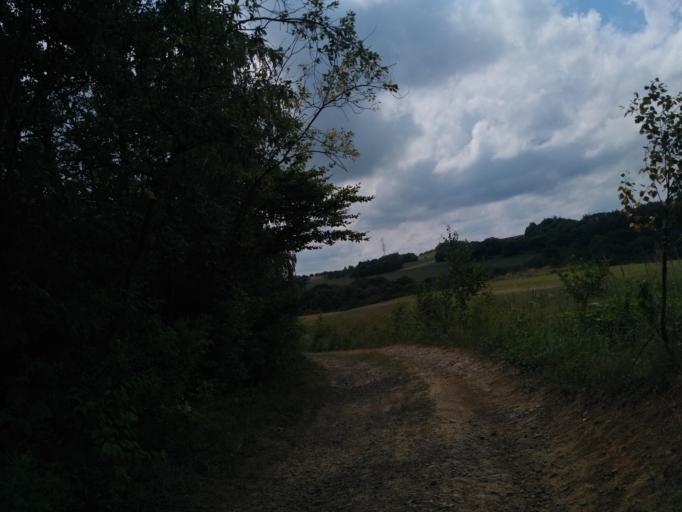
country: PL
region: Subcarpathian Voivodeship
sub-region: Powiat krosnienski
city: Iwonicz-Zdroj
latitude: 49.5853
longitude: 21.7754
